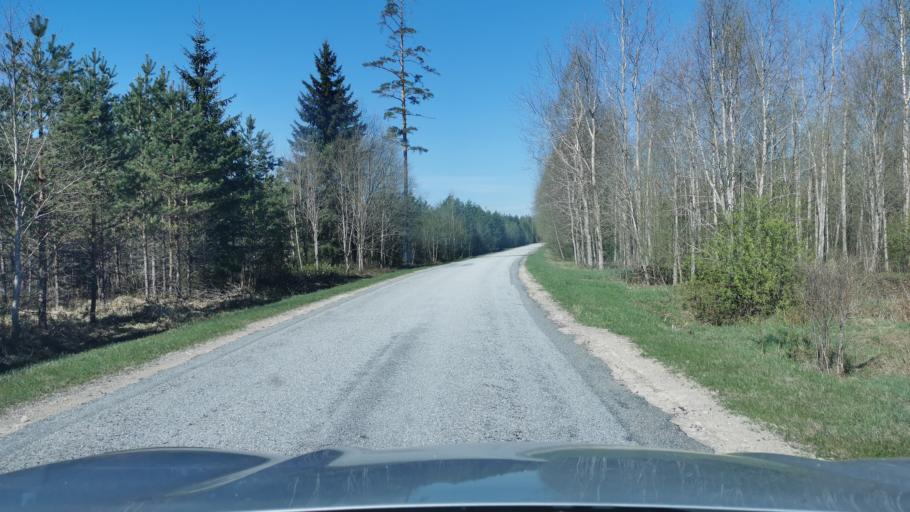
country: EE
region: Laeaene-Virumaa
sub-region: Vinni vald
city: Vinni
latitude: 59.0417
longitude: 26.6367
